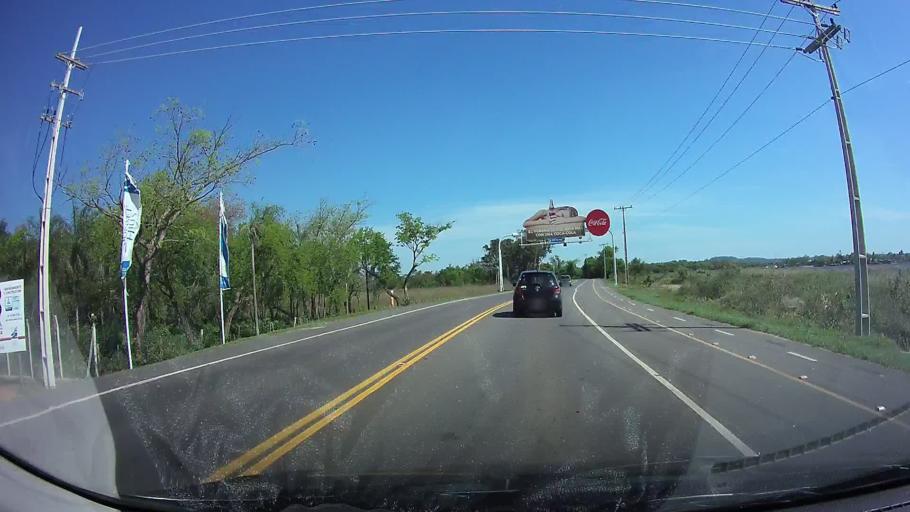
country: PY
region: Cordillera
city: San Bernardino
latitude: -25.2749
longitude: -57.3177
